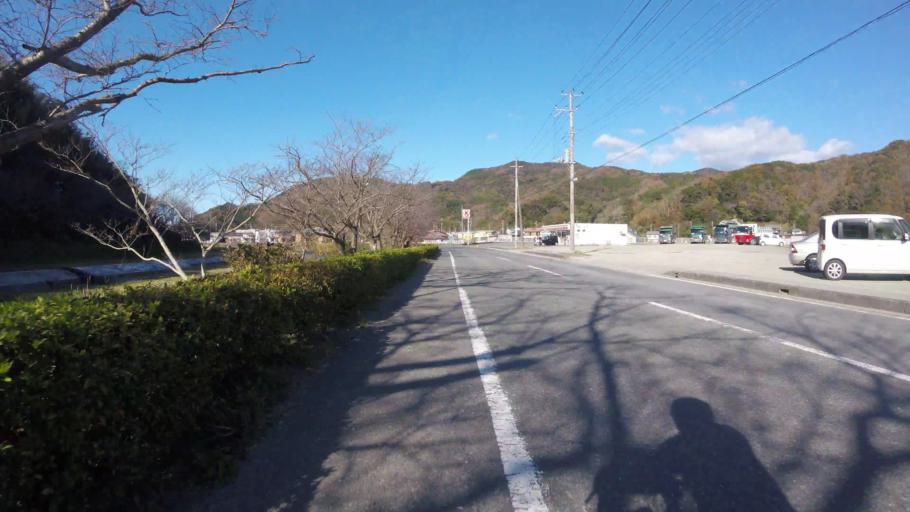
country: JP
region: Shizuoka
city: Shimoda
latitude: 34.7535
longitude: 138.7952
